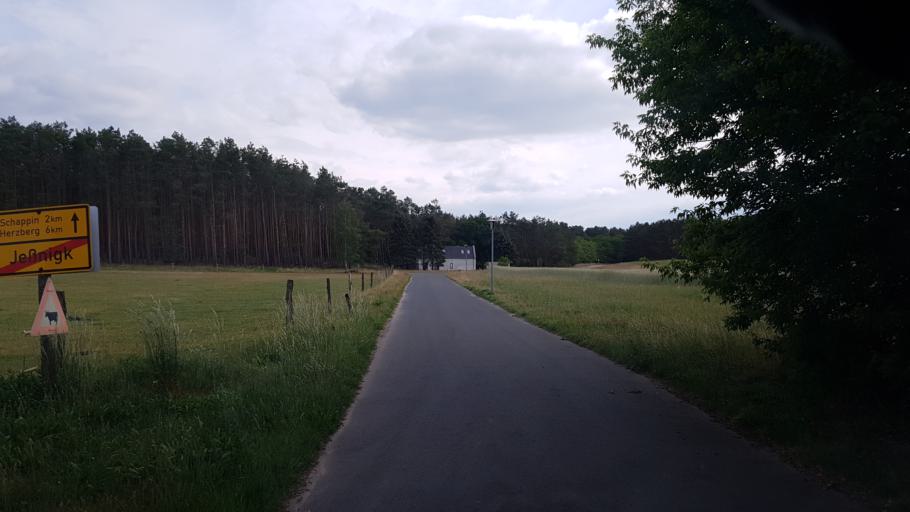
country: DE
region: Brandenburg
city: Herzberg
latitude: 51.7455
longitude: 13.2805
